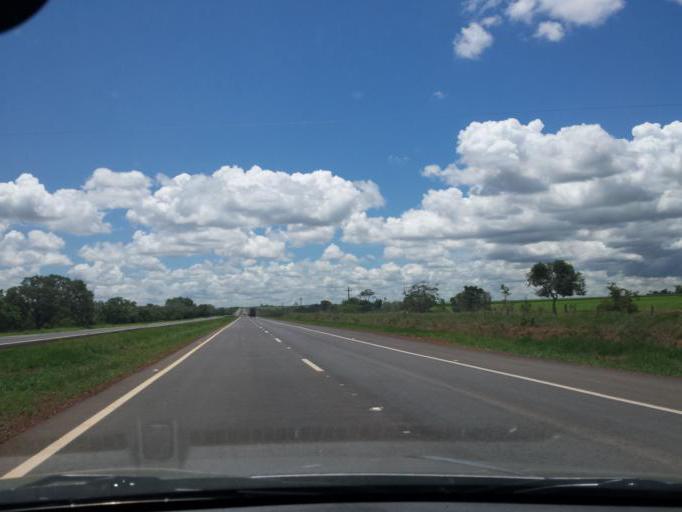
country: BR
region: Goias
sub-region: Cristalina
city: Cristalina
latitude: -16.6793
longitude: -47.7066
